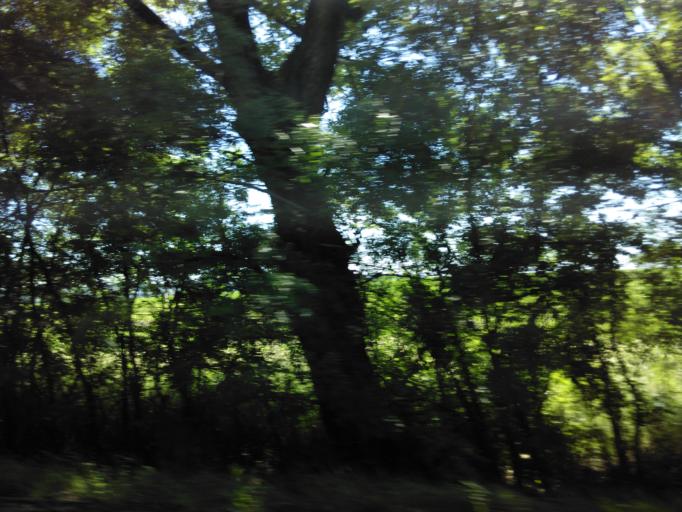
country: HU
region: Fejer
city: Bodajk
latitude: 47.3440
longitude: 18.2352
